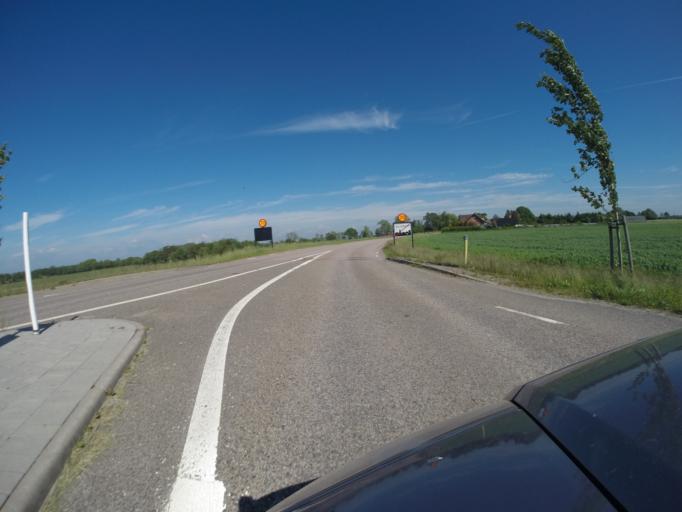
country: SE
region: Skane
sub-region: Helsingborg
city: Odakra
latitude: 56.1111
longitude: 12.6996
